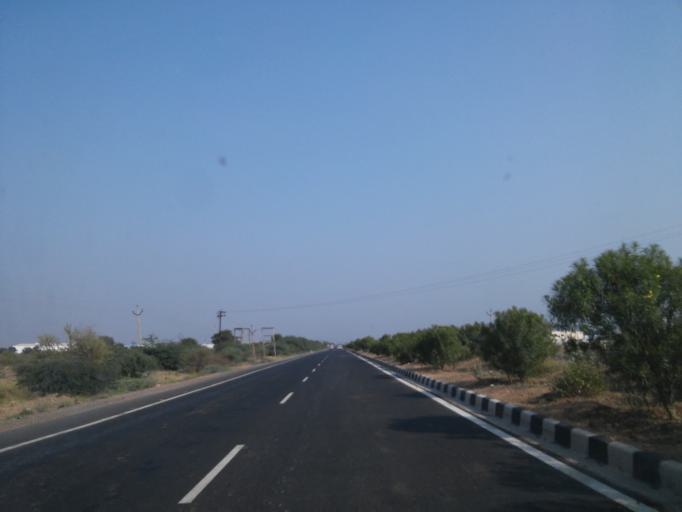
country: IN
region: Gujarat
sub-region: Surendranagar
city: Halvad
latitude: 23.0048
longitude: 71.1483
